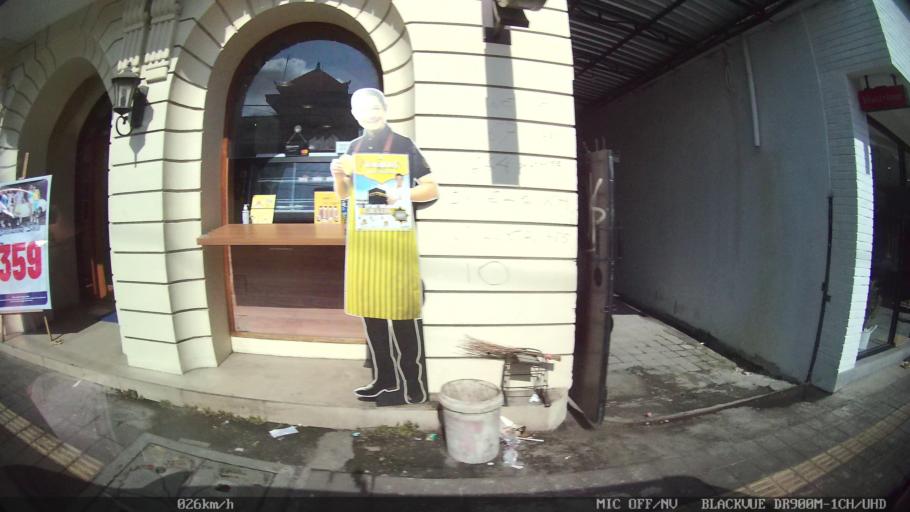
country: ID
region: Bali
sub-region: Kabupaten Gianyar
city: Ubud
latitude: -8.5086
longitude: 115.2623
